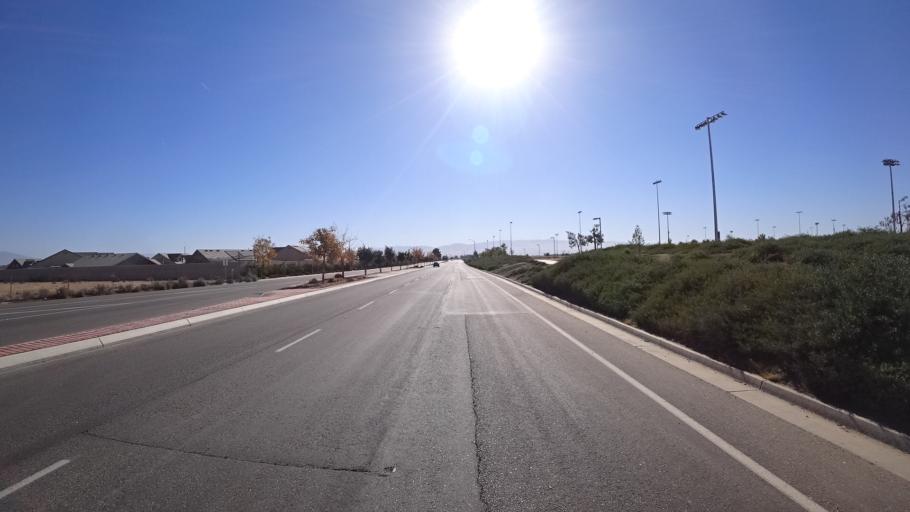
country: US
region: California
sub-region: Kern County
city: Greenfield
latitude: 35.2737
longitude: -119.0746
